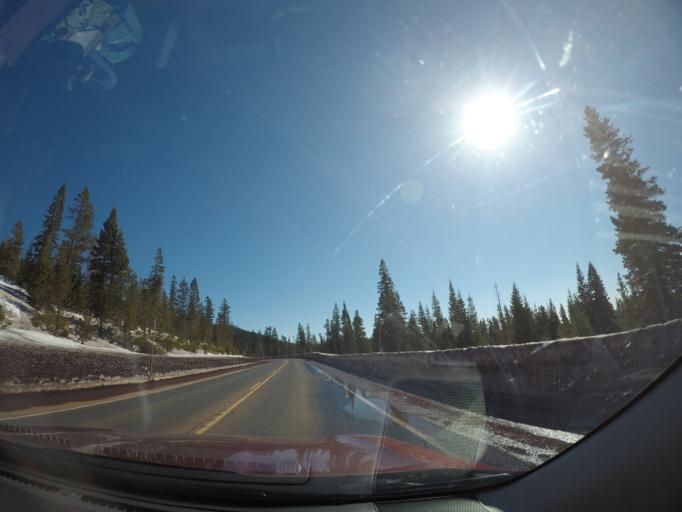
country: US
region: Oregon
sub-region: Deschutes County
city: Sunriver
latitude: 43.9831
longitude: -121.5981
